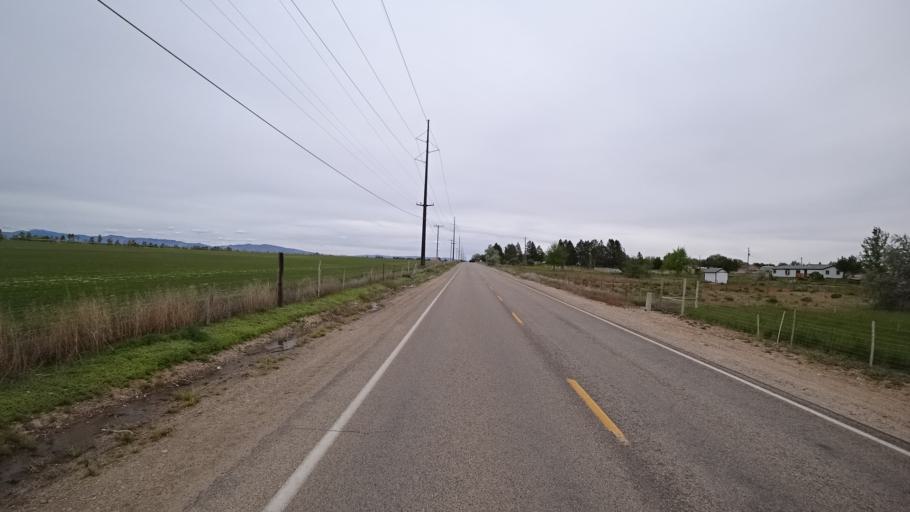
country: US
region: Idaho
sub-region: Ada County
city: Kuna
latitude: 43.4883
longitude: -116.3284
